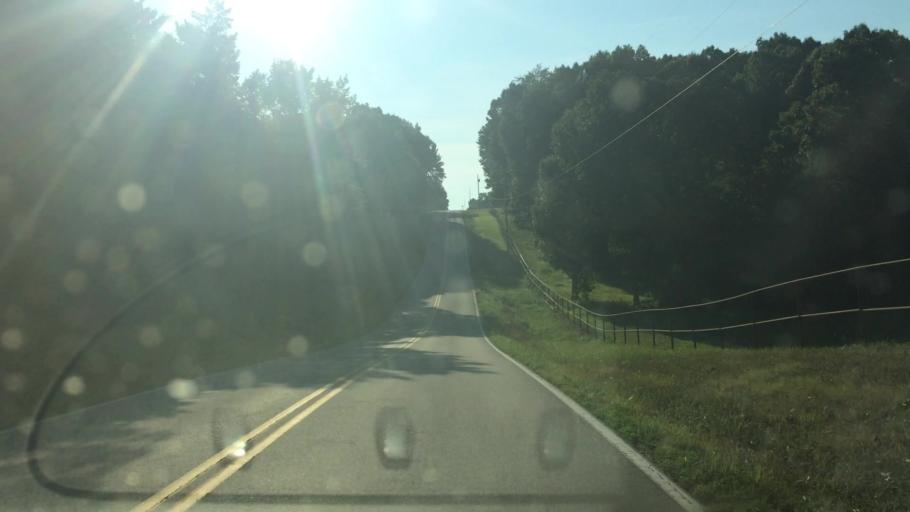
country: US
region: Missouri
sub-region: Greene County
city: Strafford
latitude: 37.2722
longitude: -93.2034
